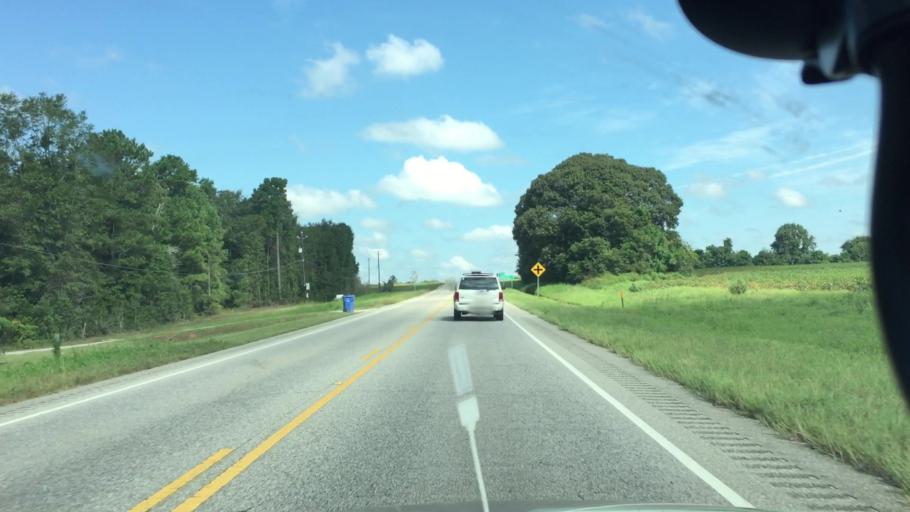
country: US
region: Alabama
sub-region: Coffee County
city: New Brockton
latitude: 31.4128
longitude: -85.8842
